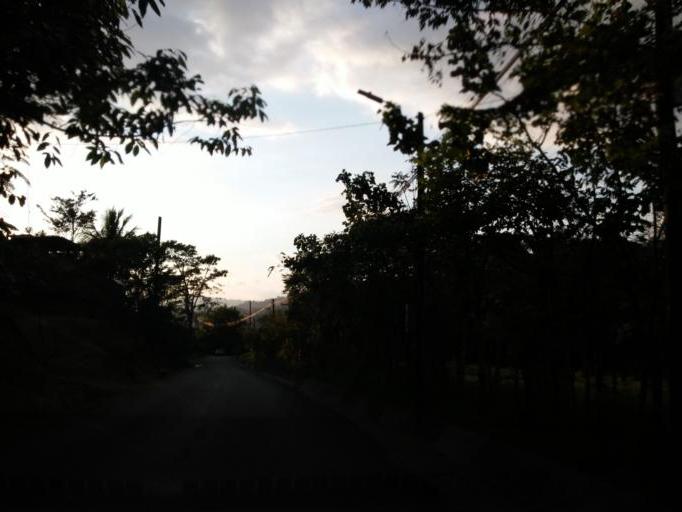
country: CR
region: San Jose
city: Palmichal
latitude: 9.8484
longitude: -84.2286
